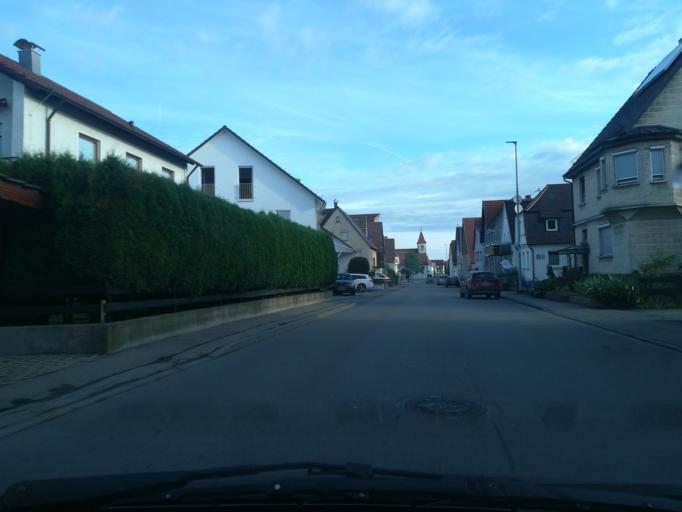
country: DE
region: Baden-Wuerttemberg
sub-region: Tuebingen Region
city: Sickenhausen
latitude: 48.5207
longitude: 9.1756
